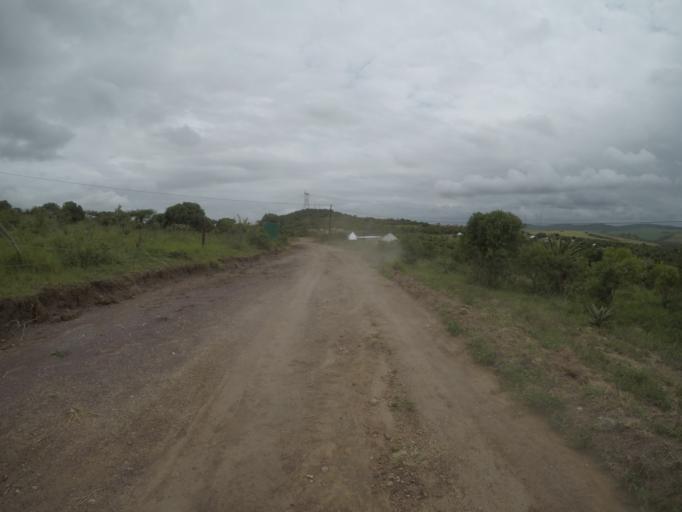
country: ZA
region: KwaZulu-Natal
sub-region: uThungulu District Municipality
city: Empangeni
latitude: -28.6046
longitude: 31.8329
